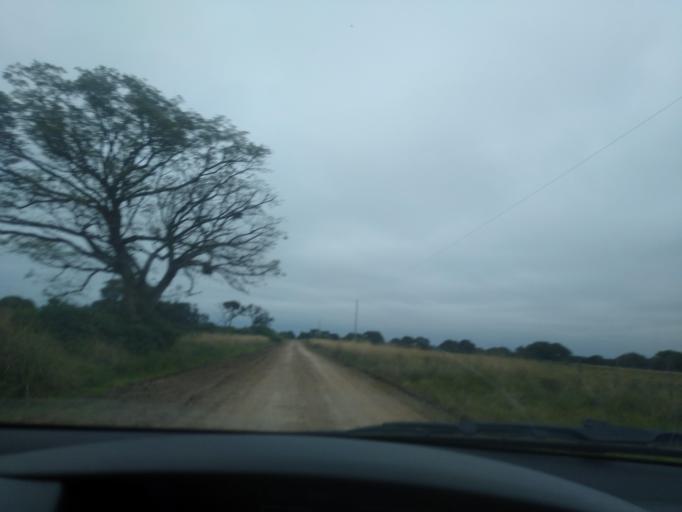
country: AR
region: Chaco
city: Colonia Benitez
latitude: -27.3644
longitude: -58.9550
